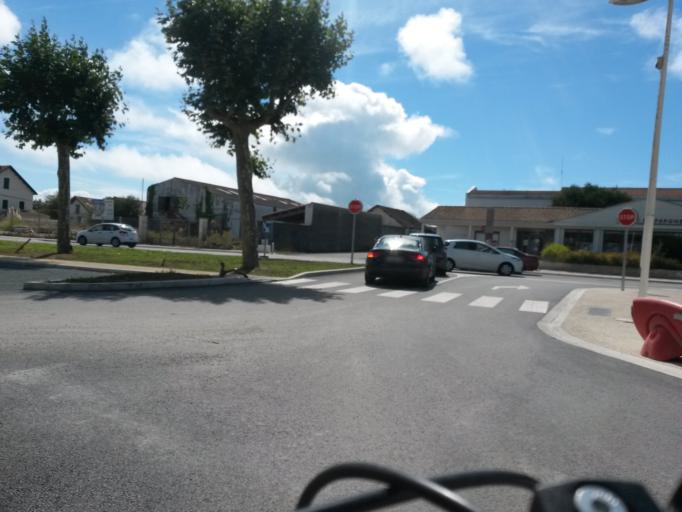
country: FR
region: Poitou-Charentes
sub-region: Departement de la Charente-Maritime
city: Dolus-d'Oleron
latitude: 45.9415
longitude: -1.3083
